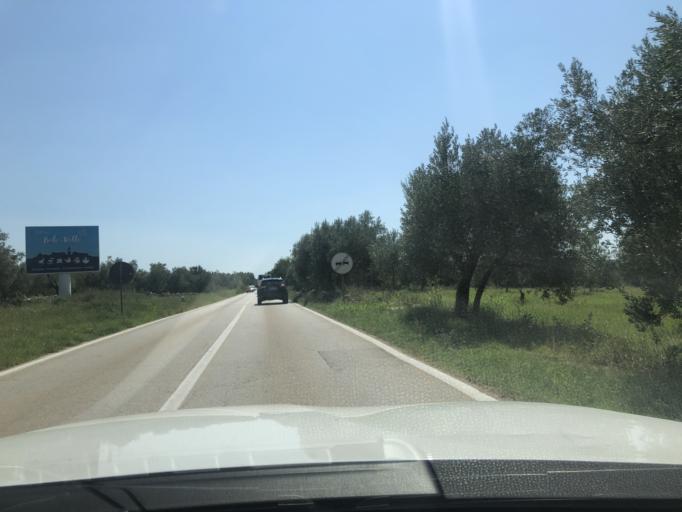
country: HR
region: Istarska
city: Vodnjan
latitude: 45.0251
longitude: 13.7997
